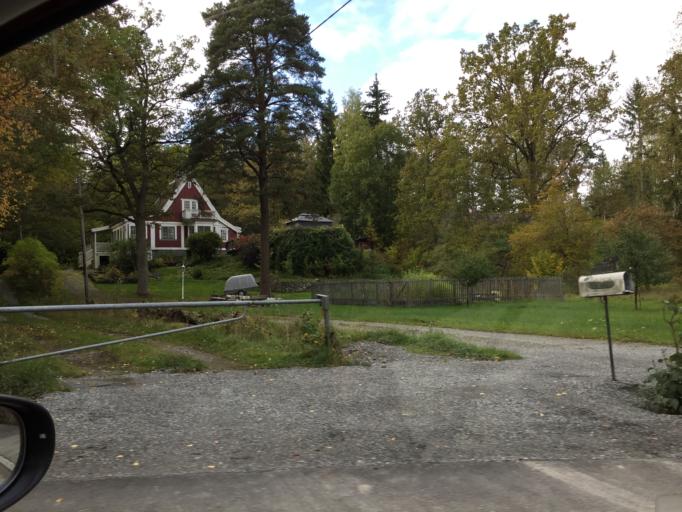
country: SE
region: Stockholm
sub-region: Salems Kommun
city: Ronninge
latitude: 59.1866
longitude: 17.7139
